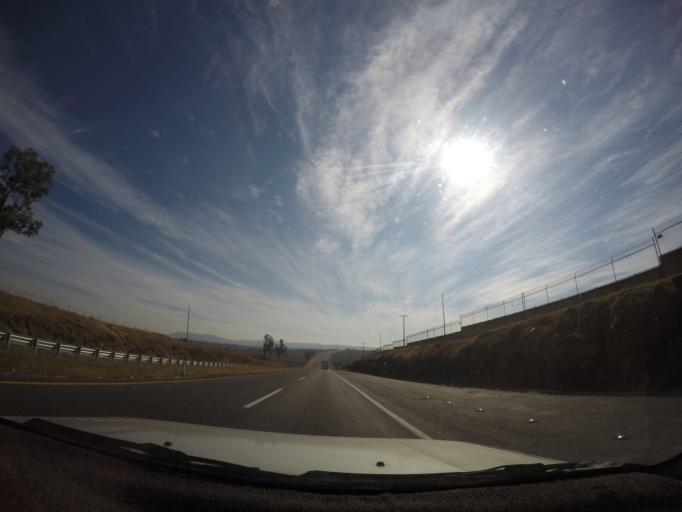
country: MX
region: Jalisco
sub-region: Zapotlanejo
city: La Mezquitera
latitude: 20.5764
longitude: -103.0892
